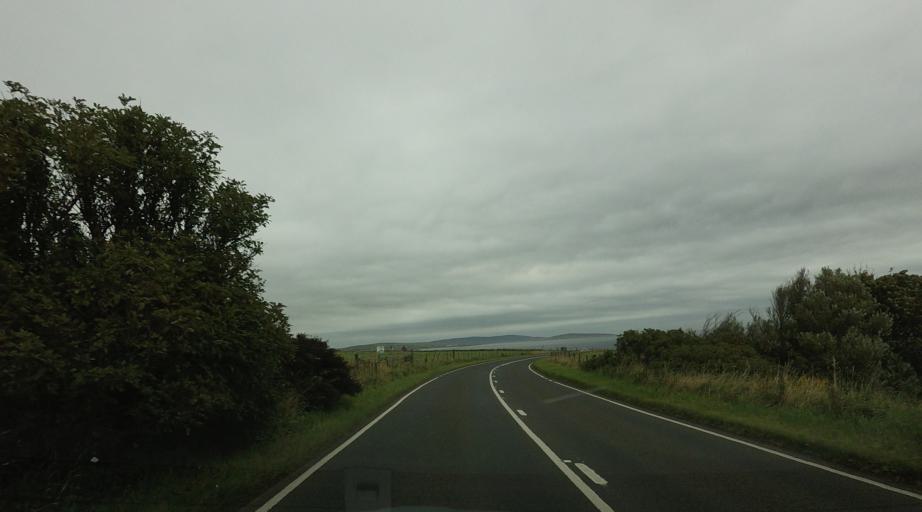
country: GB
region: Scotland
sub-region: Orkney Islands
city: Orkney
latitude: 58.9938
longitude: -2.9941
